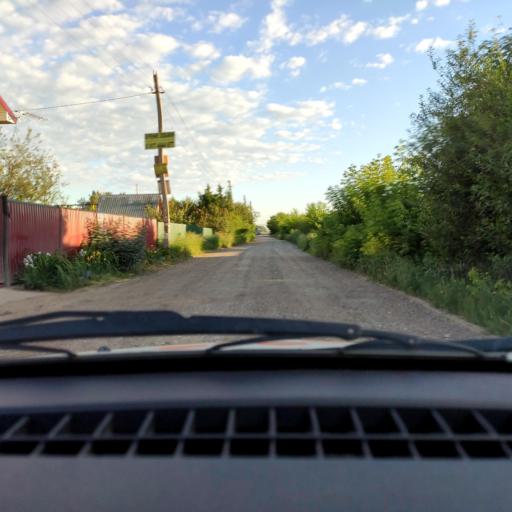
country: RU
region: Bashkortostan
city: Ufa
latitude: 54.5563
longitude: 55.9277
